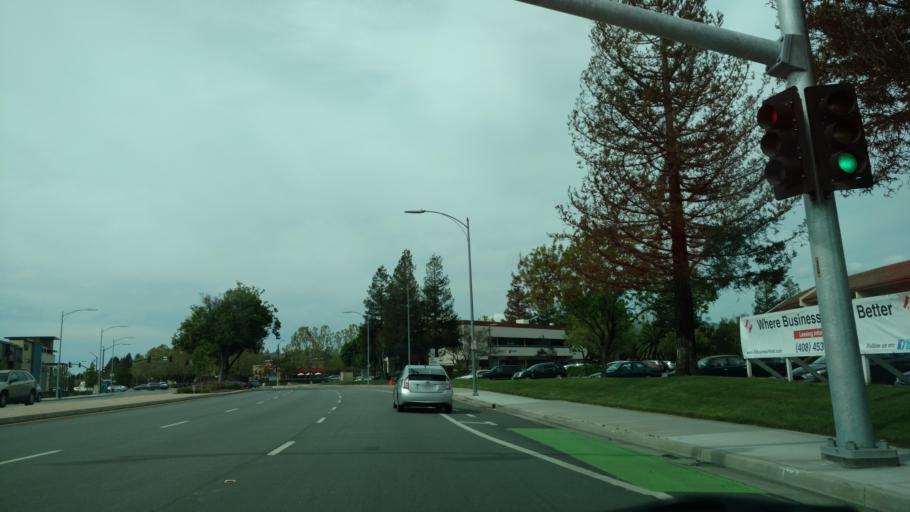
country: US
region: California
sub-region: Santa Clara County
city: San Jose
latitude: 37.3810
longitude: -121.8952
